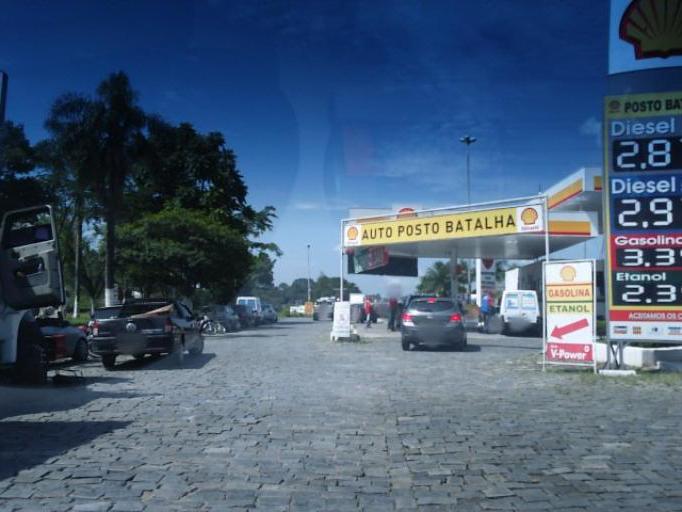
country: BR
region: Sao Paulo
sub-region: Itapecerica Da Serra
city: Itapecerica da Serra
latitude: -23.7151
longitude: -46.8804
